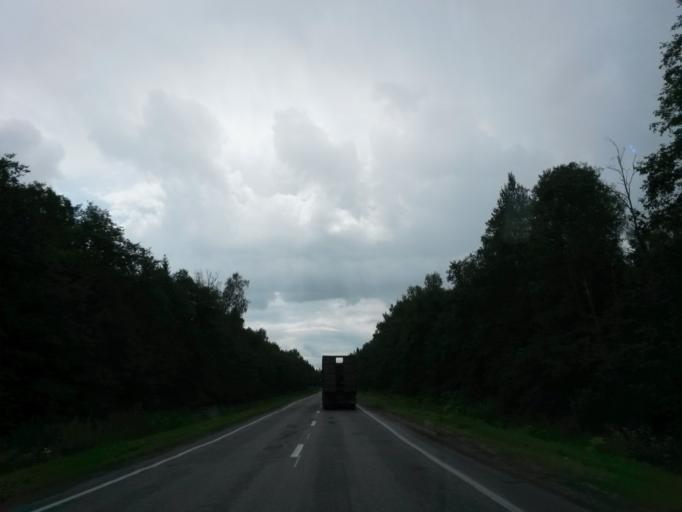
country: RU
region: Jaroslavl
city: Gavrilov-Yam
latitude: 57.4351
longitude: 39.9178
